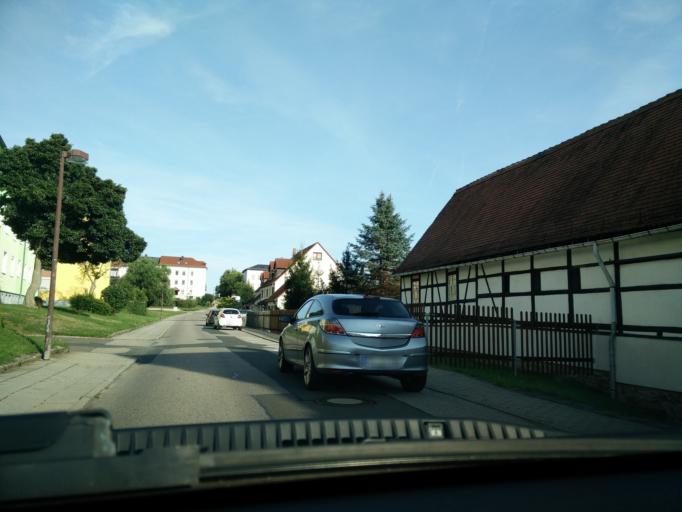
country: DE
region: Saxony
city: Geithain
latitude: 51.0566
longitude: 12.6928
